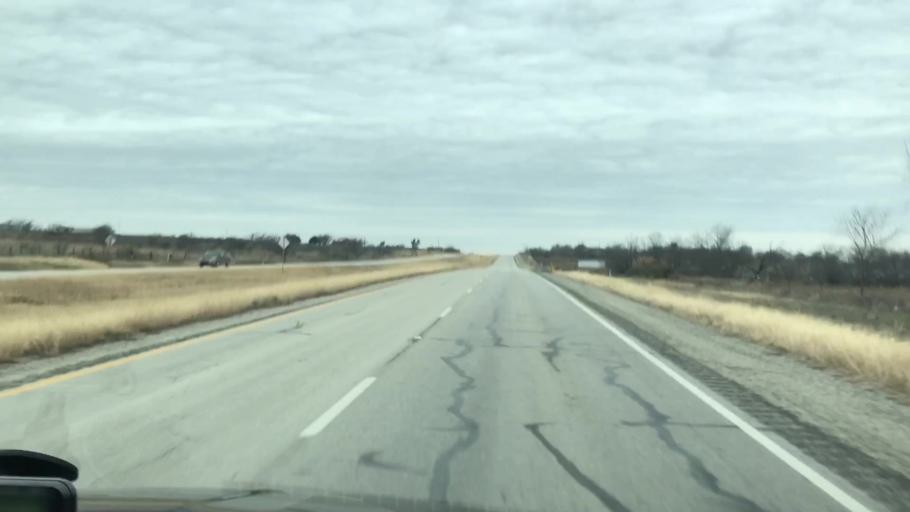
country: US
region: Texas
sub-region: Jack County
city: Jacksboro
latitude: 33.2414
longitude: -98.2202
